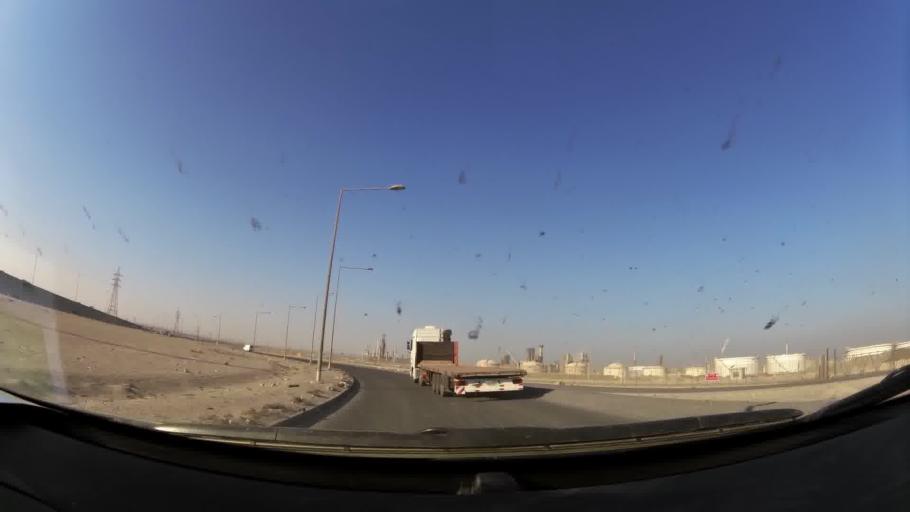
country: KW
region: Al Ahmadi
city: Al Fahahil
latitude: 29.0120
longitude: 48.1333
